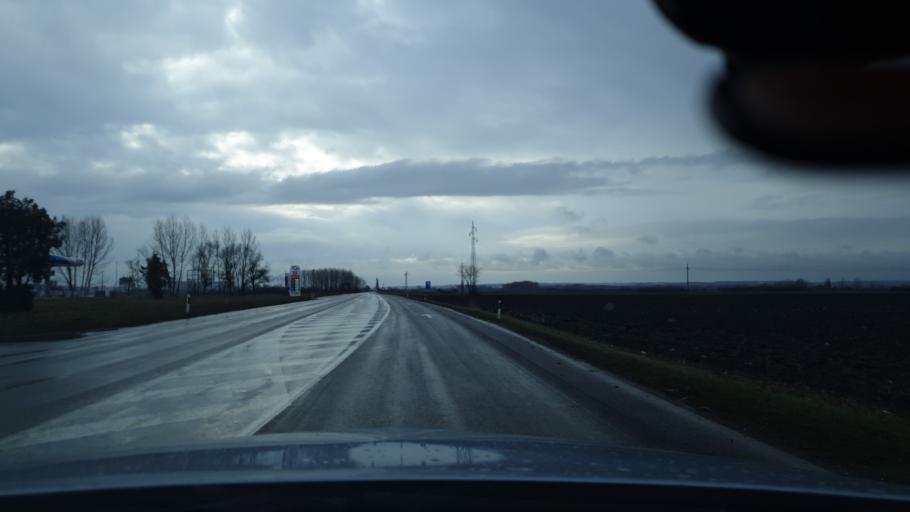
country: RS
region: Autonomna Pokrajina Vojvodina
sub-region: Juznobanatski Okrug
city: Kovin
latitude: 44.7337
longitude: 20.9654
